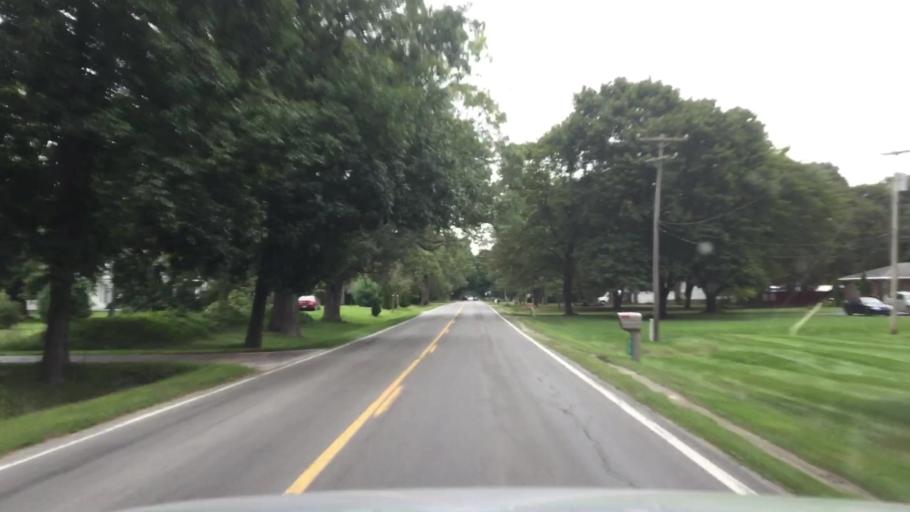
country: US
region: Michigan
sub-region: Washtenaw County
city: Ypsilanti
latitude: 42.1657
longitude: -83.6480
